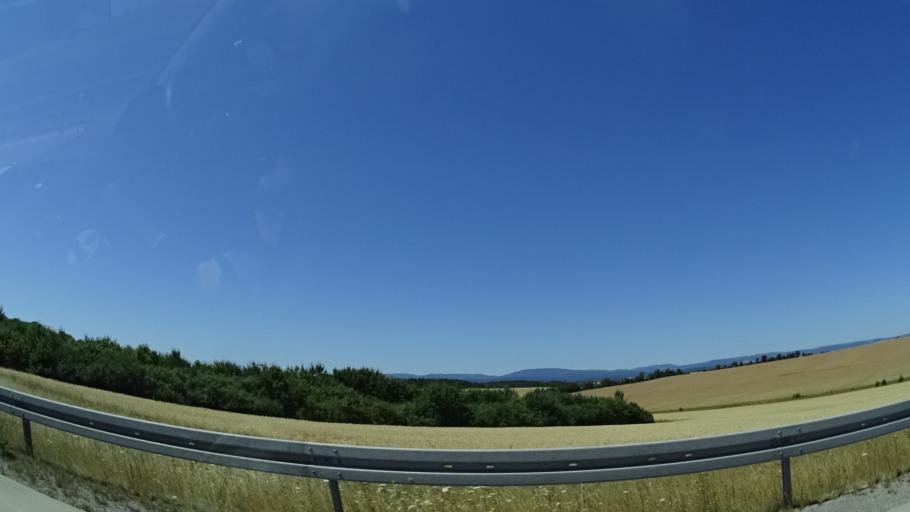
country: DE
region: Bavaria
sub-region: Regierungsbezirk Unterfranken
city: Rodelmaier
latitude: 50.3047
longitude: 10.2795
